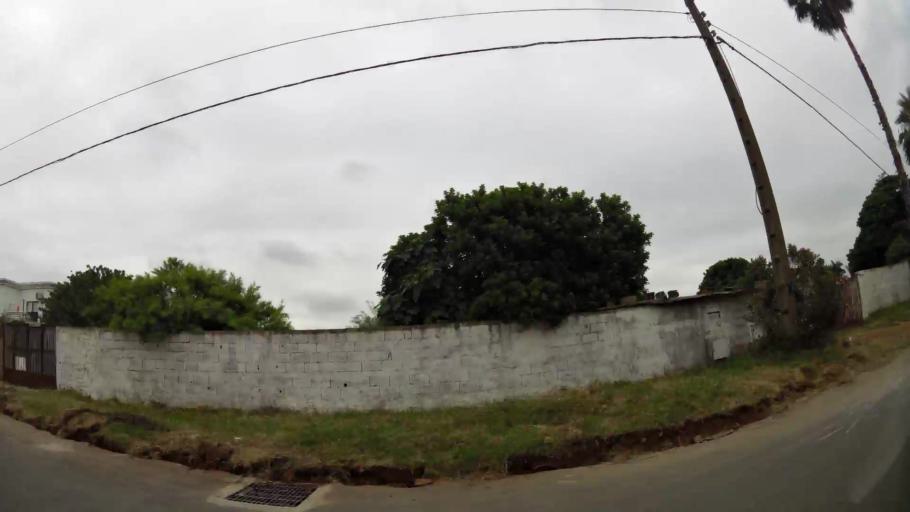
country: MA
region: Rabat-Sale-Zemmour-Zaer
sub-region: Rabat
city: Rabat
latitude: 33.9650
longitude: -6.8150
